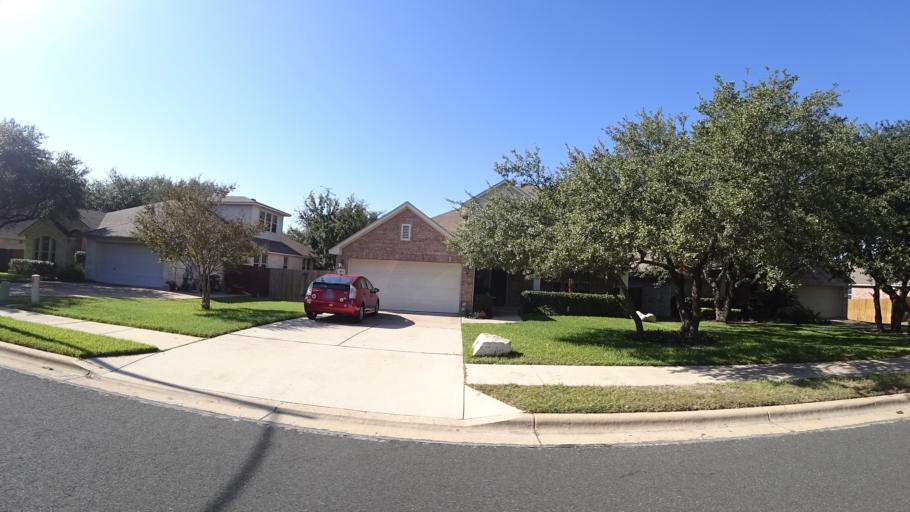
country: US
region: Texas
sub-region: Travis County
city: Shady Hollow
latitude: 30.1982
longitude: -97.8527
